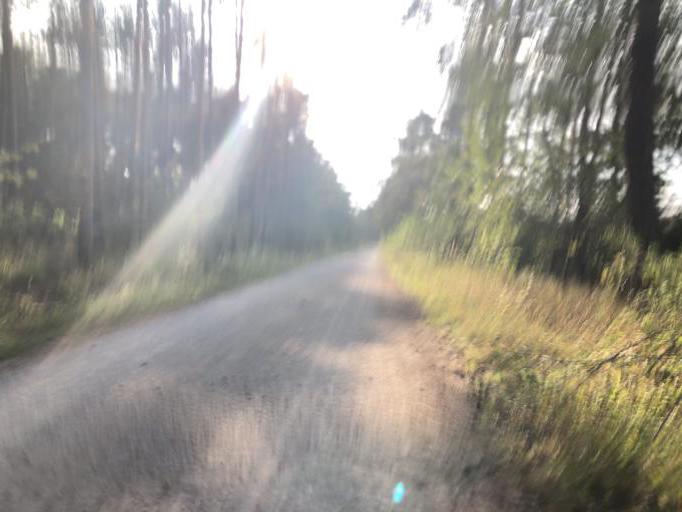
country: DE
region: Bavaria
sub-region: Regierungsbezirk Mittelfranken
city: Uttenreuth
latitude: 49.5778
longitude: 11.0936
